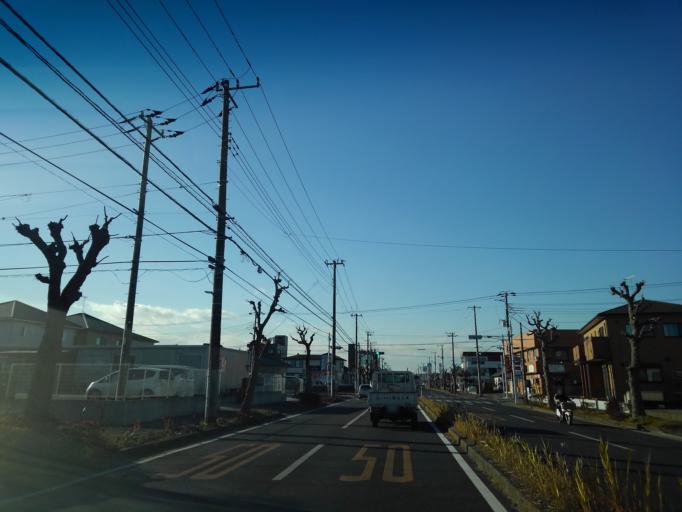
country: JP
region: Chiba
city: Kimitsu
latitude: 35.3299
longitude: 139.8955
